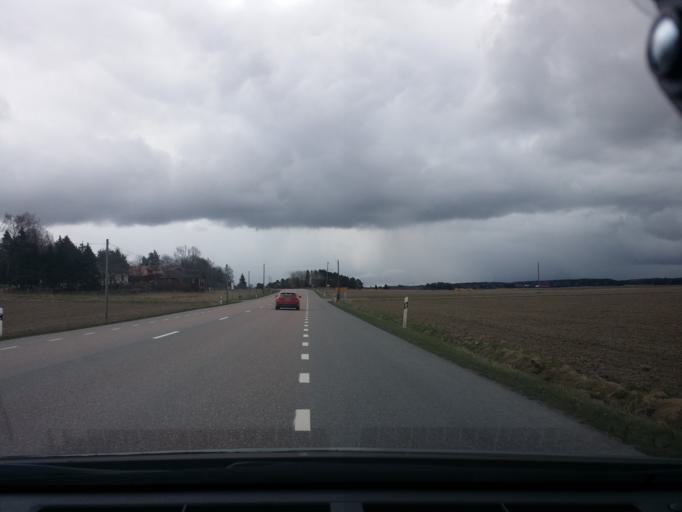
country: SE
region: Uppsala
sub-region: Enkopings Kommun
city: Irsta
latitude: 59.7614
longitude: 16.9218
